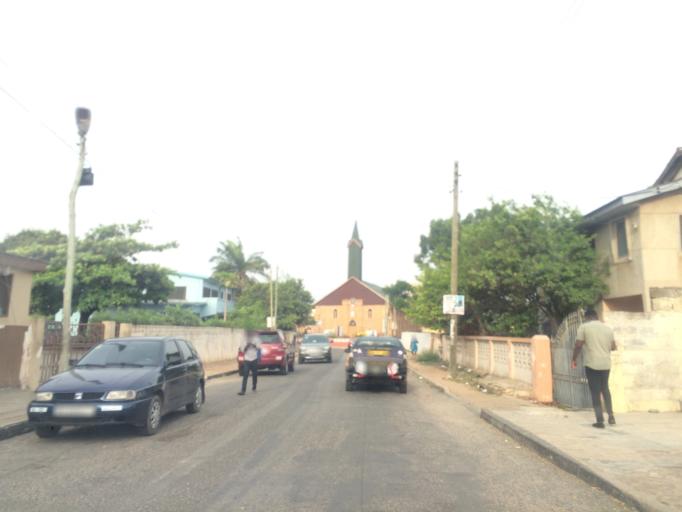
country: GH
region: Greater Accra
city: Accra
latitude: 5.5539
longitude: -0.1857
